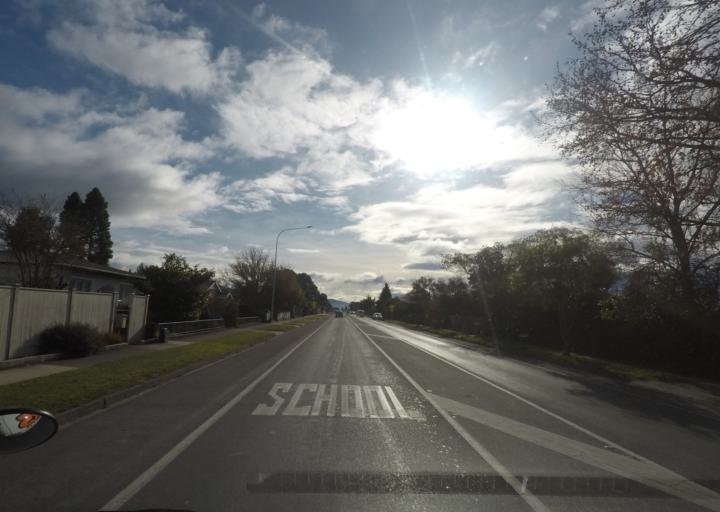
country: NZ
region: Tasman
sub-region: Tasman District
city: Motueka
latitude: -41.1287
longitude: 173.0102
